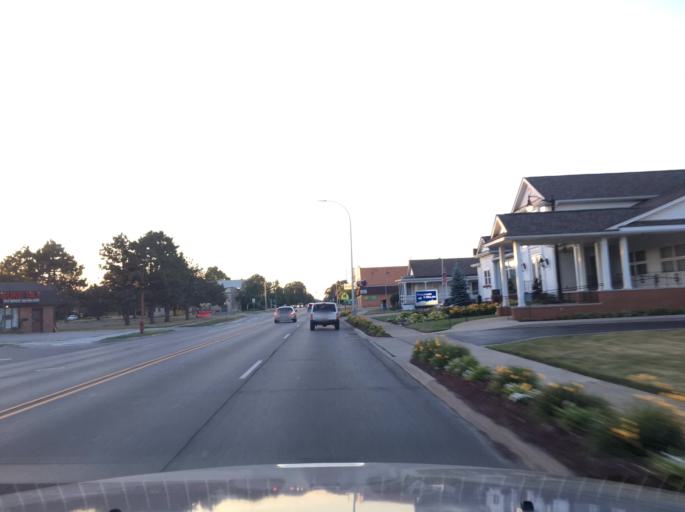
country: US
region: Michigan
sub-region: Macomb County
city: Fraser
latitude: 42.5372
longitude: -82.9518
